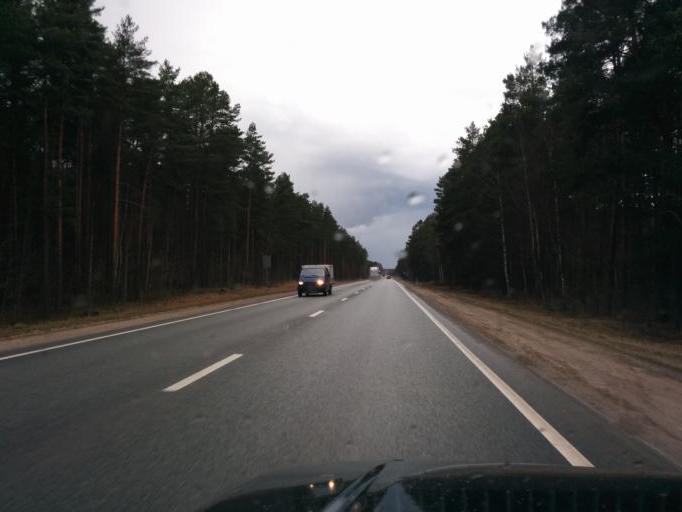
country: LV
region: Babite
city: Pinki
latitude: 56.8873
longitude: 23.9412
